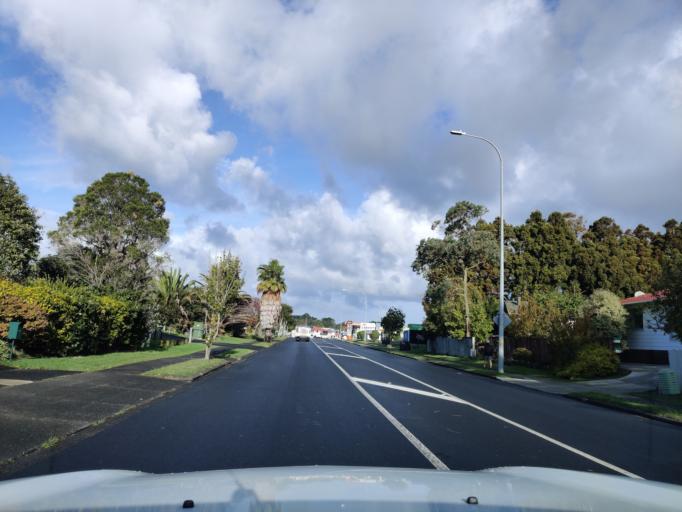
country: NZ
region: Auckland
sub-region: Auckland
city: Pakuranga
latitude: -36.9121
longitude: 174.9011
